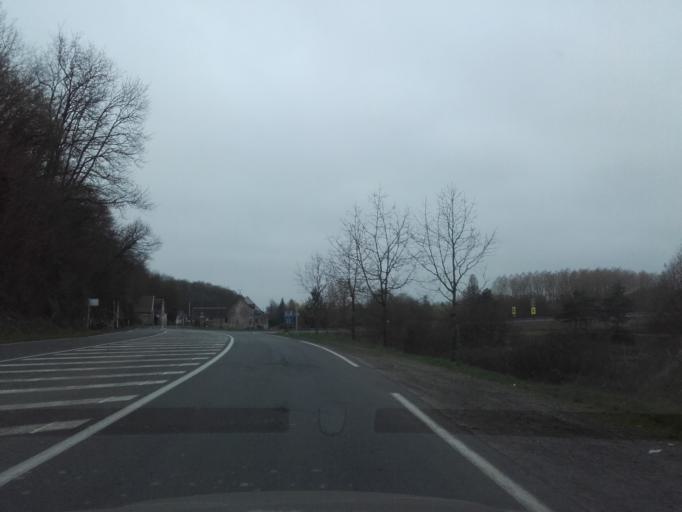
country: FR
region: Centre
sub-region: Departement d'Indre-et-Loire
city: Cinq-Mars-la-Pile
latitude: 47.3262
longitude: 0.4771
